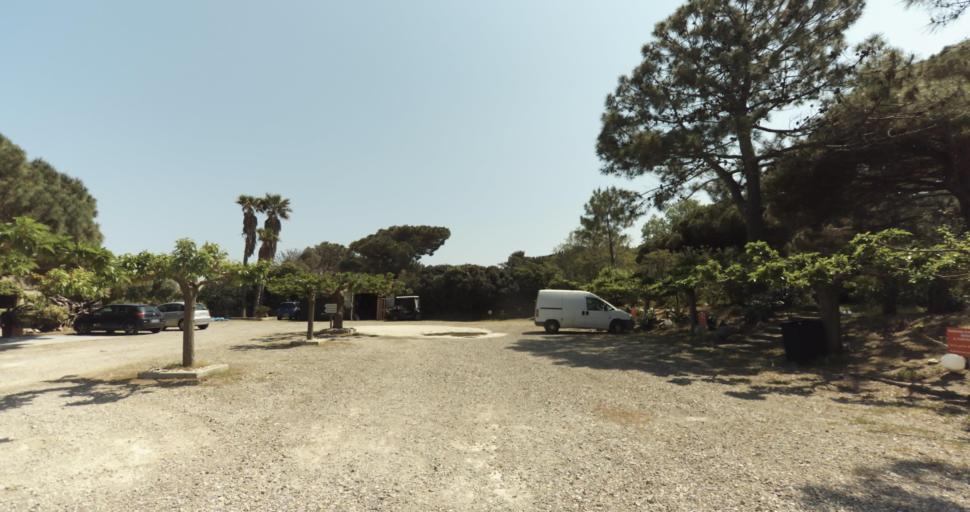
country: FR
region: Corsica
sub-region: Departement de la Haute-Corse
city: Biguglia
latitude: 42.6339
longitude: 9.4659
